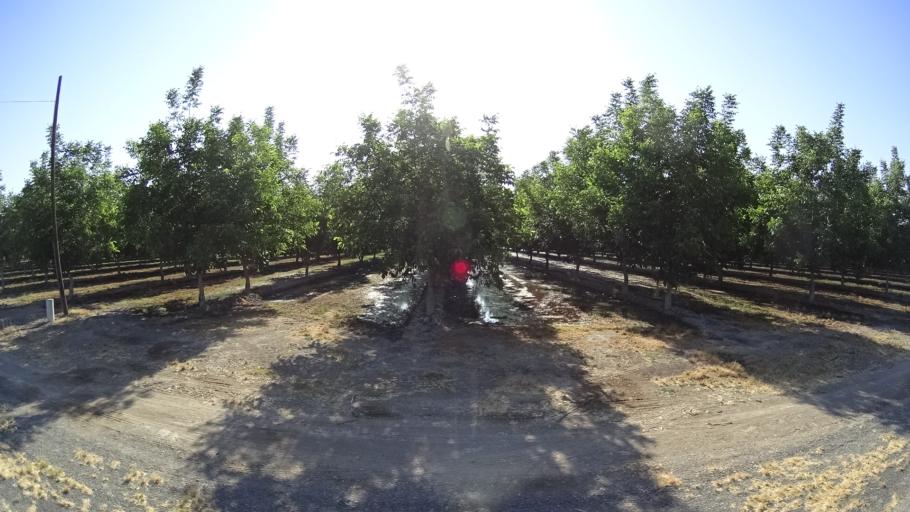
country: US
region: California
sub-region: Kings County
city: Lucerne
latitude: 36.3844
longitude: -119.7090
